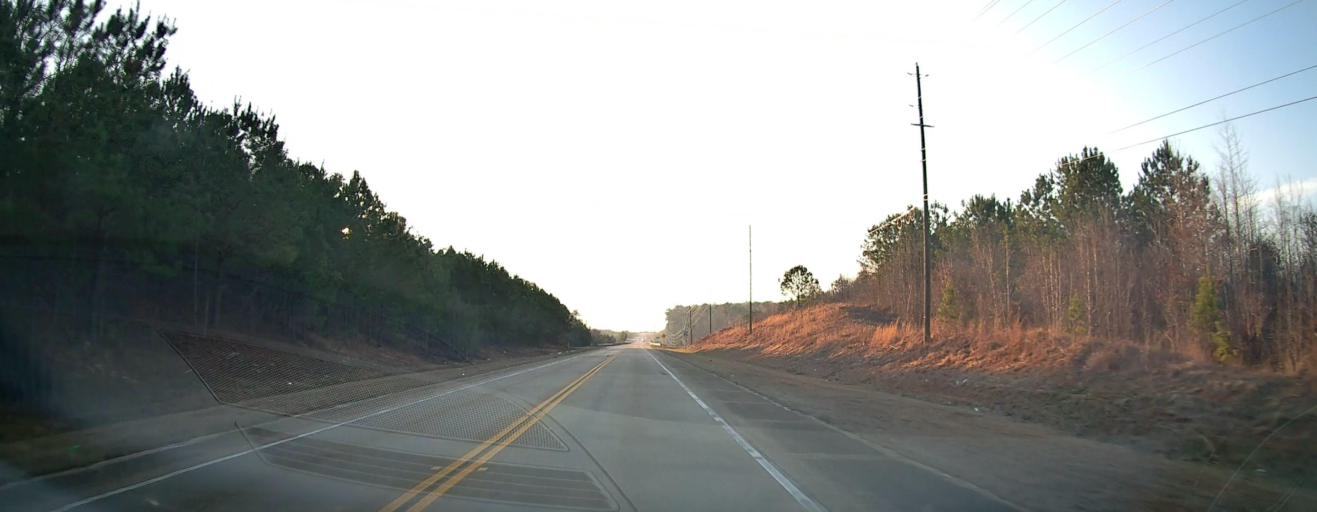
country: US
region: Georgia
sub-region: Troup County
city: La Grange
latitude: 32.9894
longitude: -85.0555
